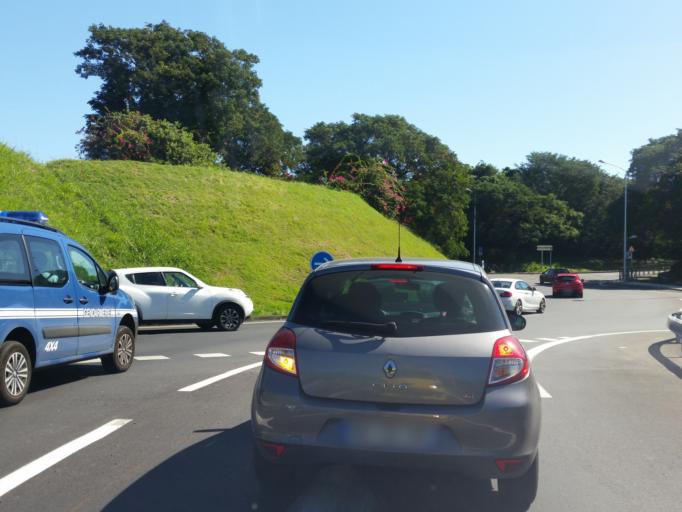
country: RE
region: Reunion
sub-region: Reunion
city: Sainte-Marie
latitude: -20.8984
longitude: 55.5207
